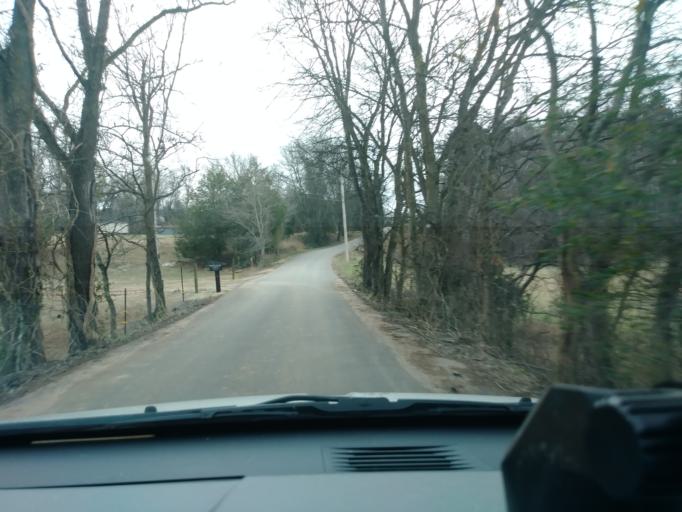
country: US
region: Tennessee
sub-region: Greene County
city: Greeneville
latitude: 36.0837
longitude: -82.8892
